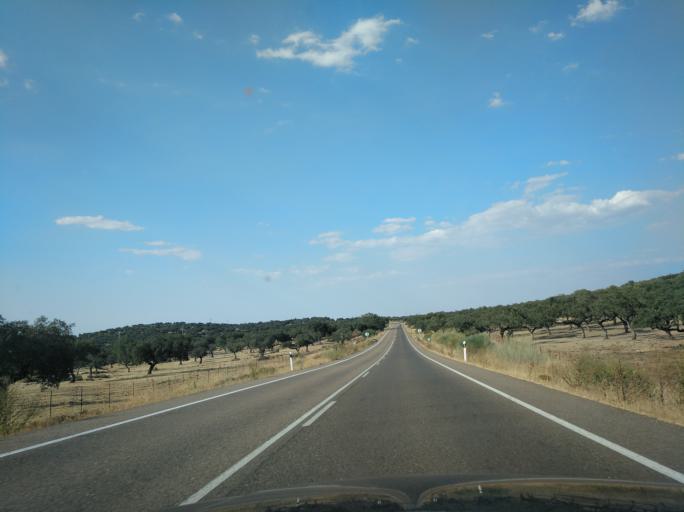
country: ES
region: Extremadura
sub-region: Provincia de Badajoz
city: Villanueva del Fresno
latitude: 38.3916
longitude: -7.1485
